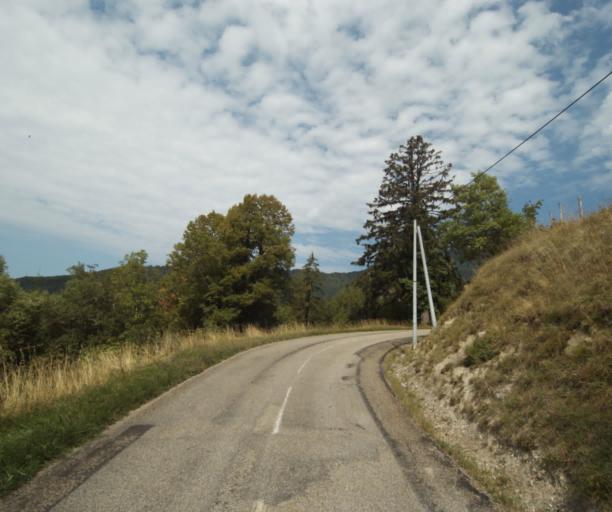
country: FR
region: Rhone-Alpes
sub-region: Departement de l'Isere
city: Le Sappey-en-Chartreuse
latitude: 45.2613
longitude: 5.7488
